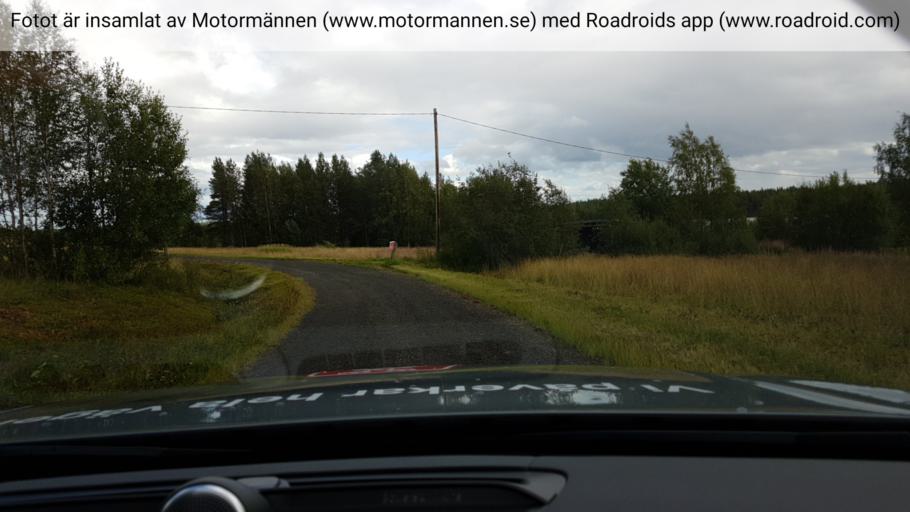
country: SE
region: Jaemtland
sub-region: Krokoms Kommun
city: Krokom
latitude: 63.7723
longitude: 14.6403
